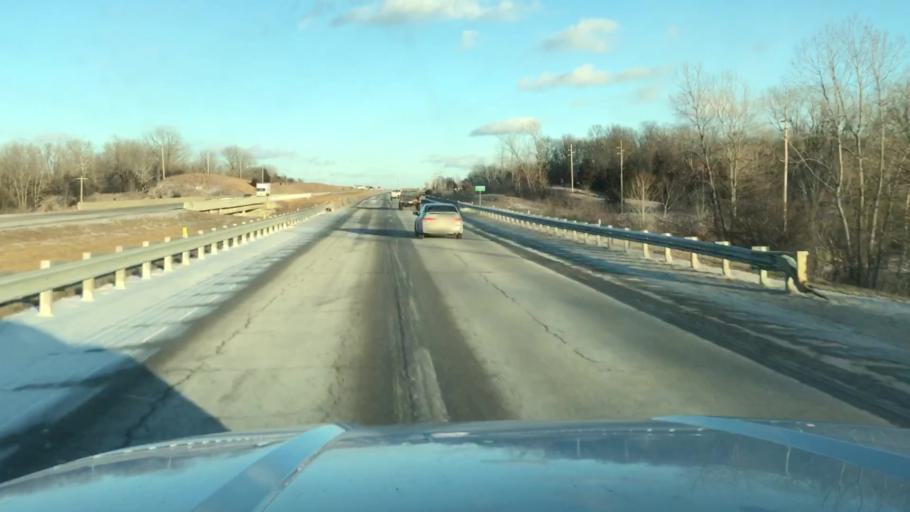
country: US
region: Missouri
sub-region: Clinton County
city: Cameron
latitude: 39.7547
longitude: -94.3176
